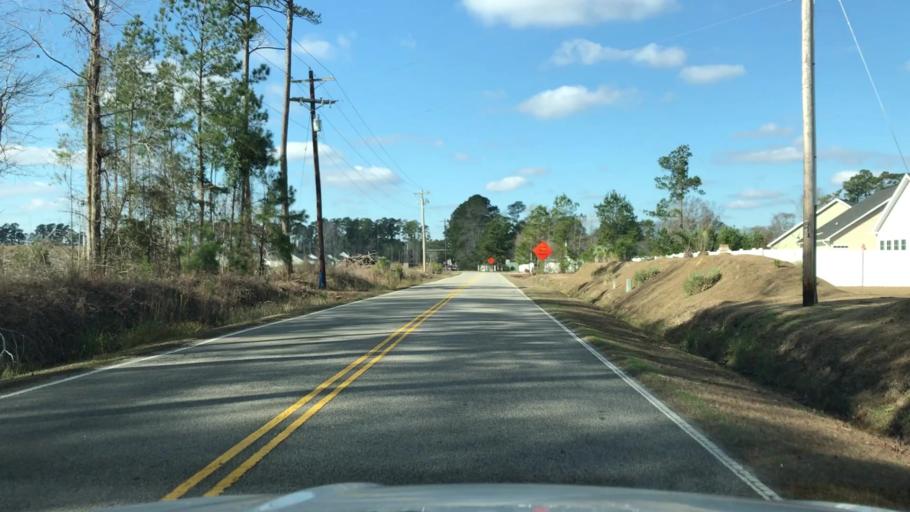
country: US
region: South Carolina
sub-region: Horry County
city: Socastee
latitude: 33.6590
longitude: -79.0054
